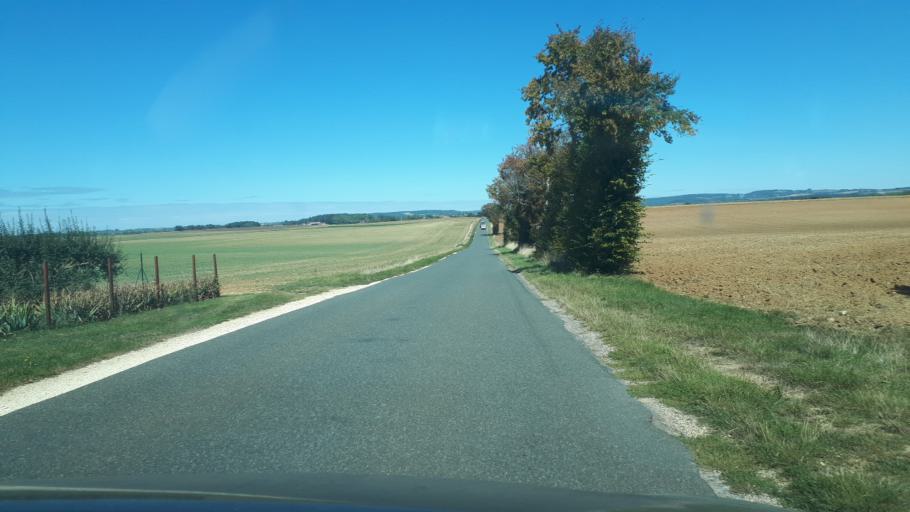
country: FR
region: Centre
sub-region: Departement du Cher
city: Sainte-Solange
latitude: 47.1644
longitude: 2.5679
